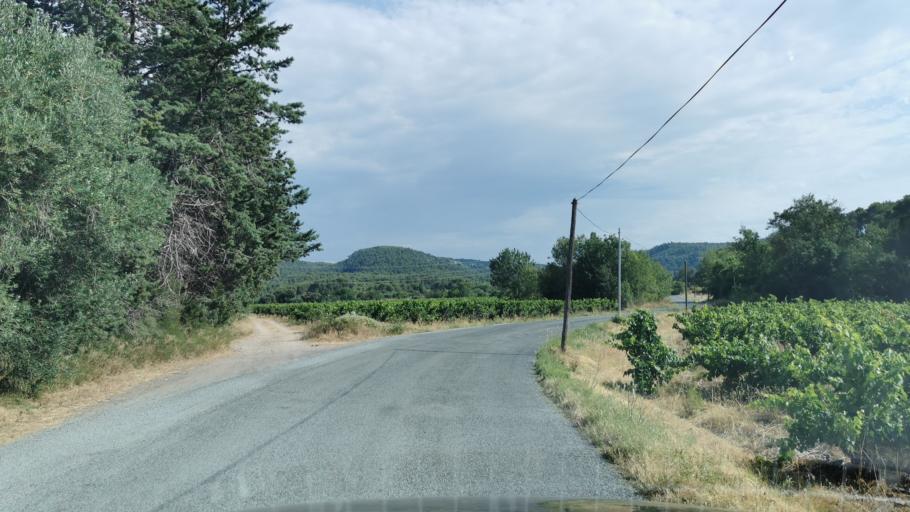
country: FR
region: Languedoc-Roussillon
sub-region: Departement de l'Aude
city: Bize-Minervois
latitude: 43.3363
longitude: 2.8766
